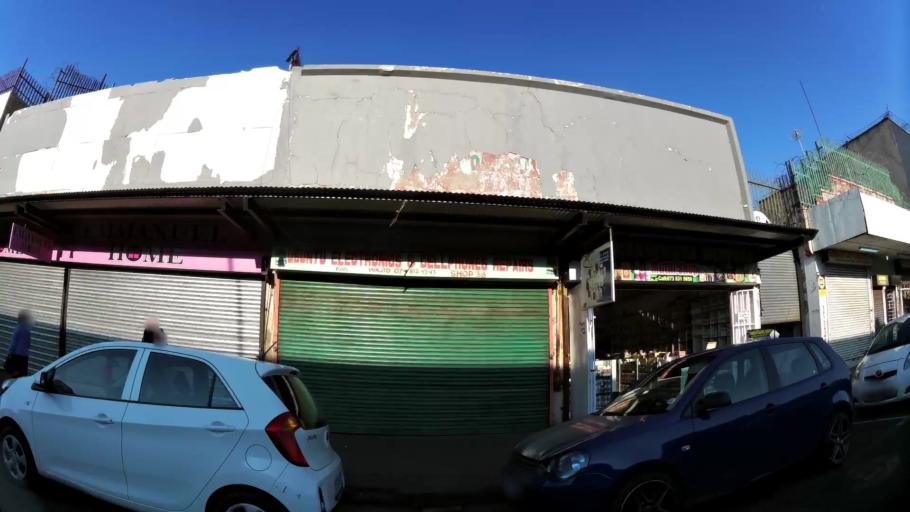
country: ZA
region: Gauteng
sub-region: Ekurhuleni Metropolitan Municipality
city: Germiston
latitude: -26.2114
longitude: 28.1677
